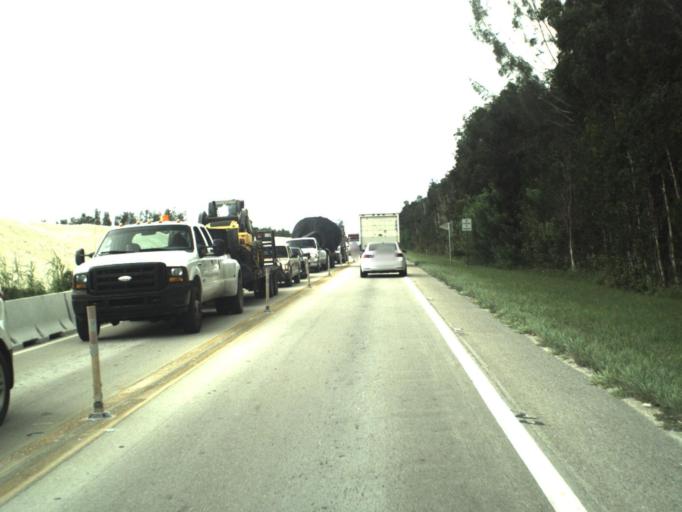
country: US
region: Florida
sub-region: Miami-Dade County
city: Kendall West
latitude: 25.7513
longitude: -80.4810
